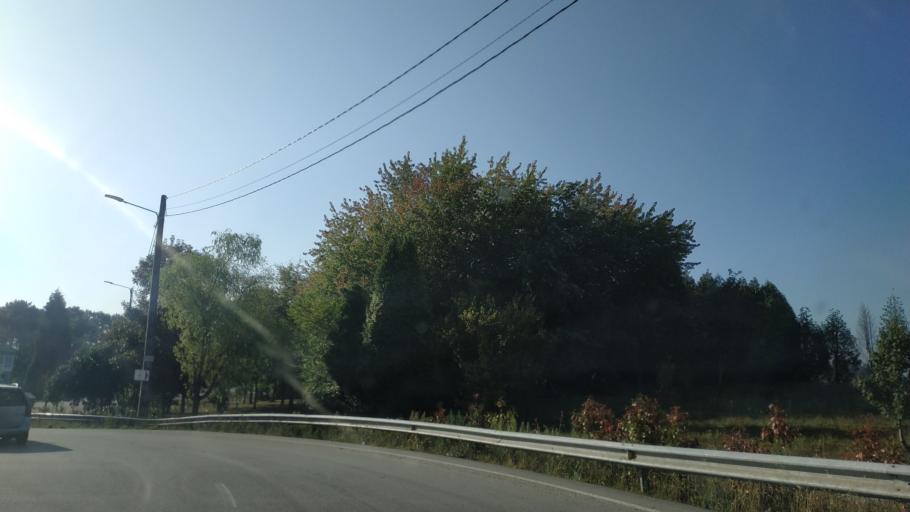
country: ES
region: Galicia
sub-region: Provincia da Coruna
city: Carballo
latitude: 43.2323
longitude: -8.6795
